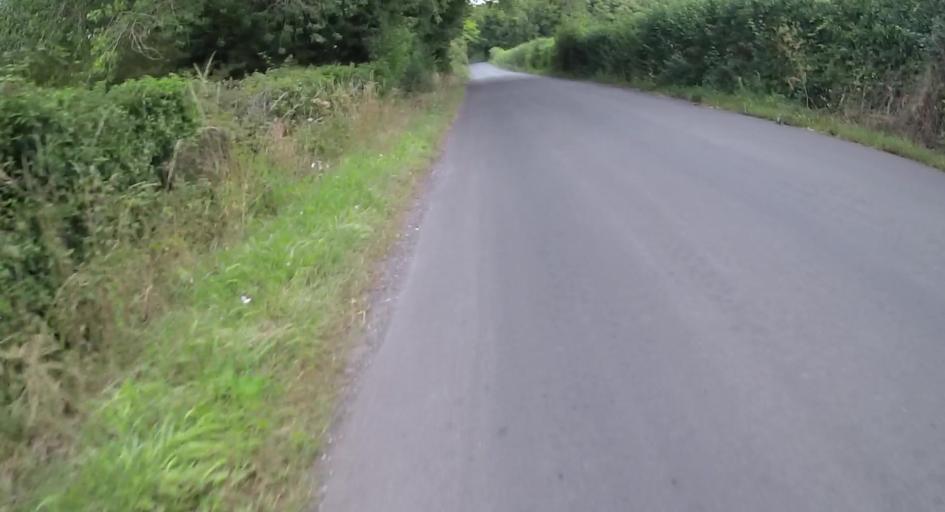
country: GB
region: England
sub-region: Hampshire
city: Kings Worthy
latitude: 51.1302
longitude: -1.3096
